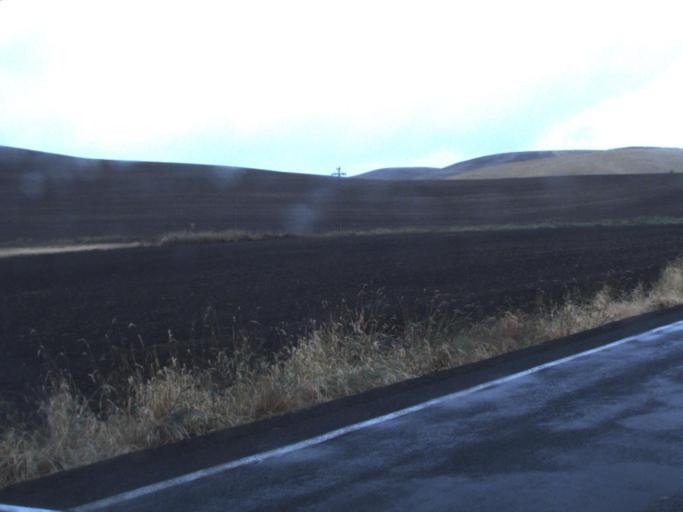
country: US
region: Washington
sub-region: Whitman County
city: Colfax
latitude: 47.0095
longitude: -117.4643
